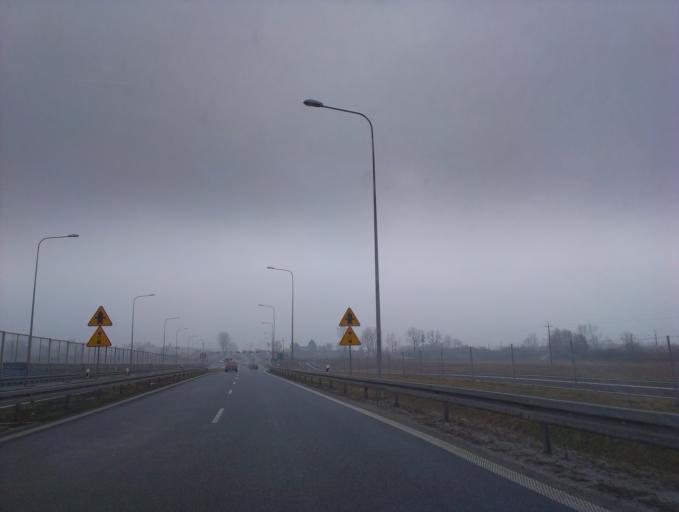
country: PL
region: Greater Poland Voivodeship
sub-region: Powiat poznanski
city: Zlotniki
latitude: 52.5155
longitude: 16.8319
